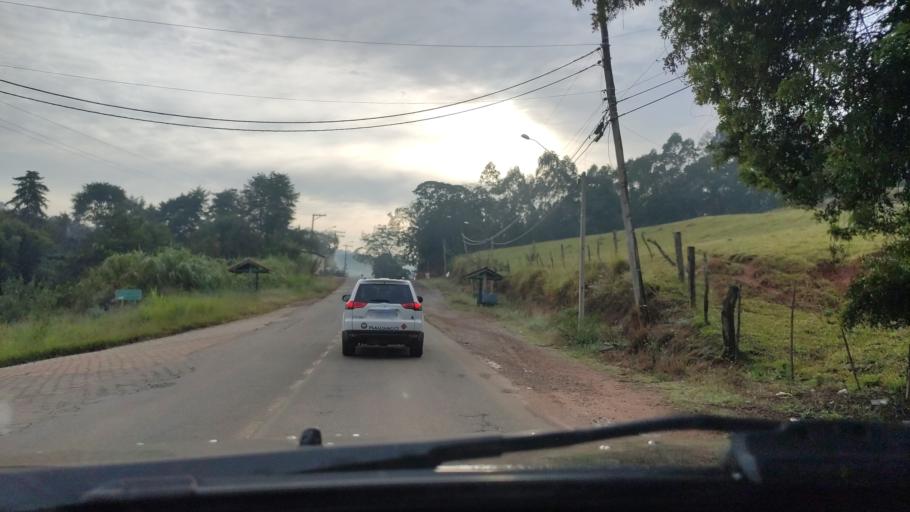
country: BR
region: Sao Paulo
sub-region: Jarinu
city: Jarinu
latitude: -23.1230
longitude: -46.7712
